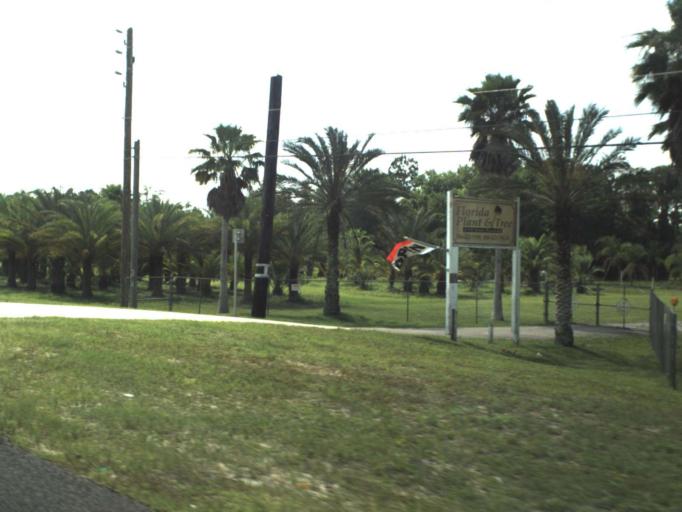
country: US
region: Florida
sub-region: Volusia County
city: Samsula-Spruce Creek
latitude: 29.0252
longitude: -81.1331
